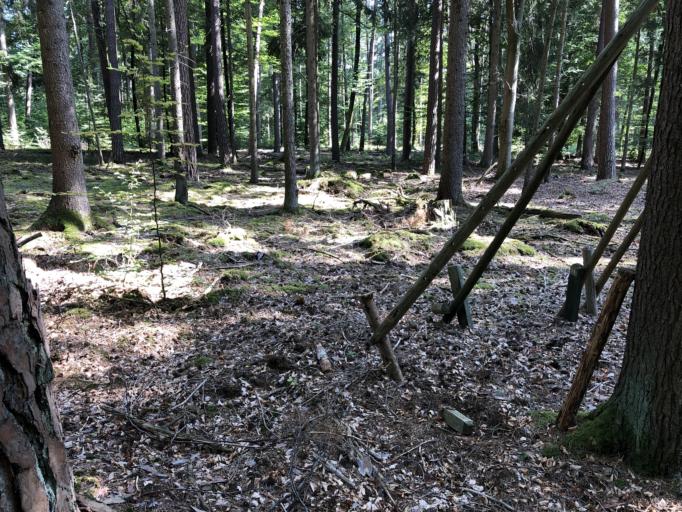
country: DE
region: Baden-Wuerttemberg
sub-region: Tuebingen Region
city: Bodelshausen
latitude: 48.4186
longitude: 8.9439
